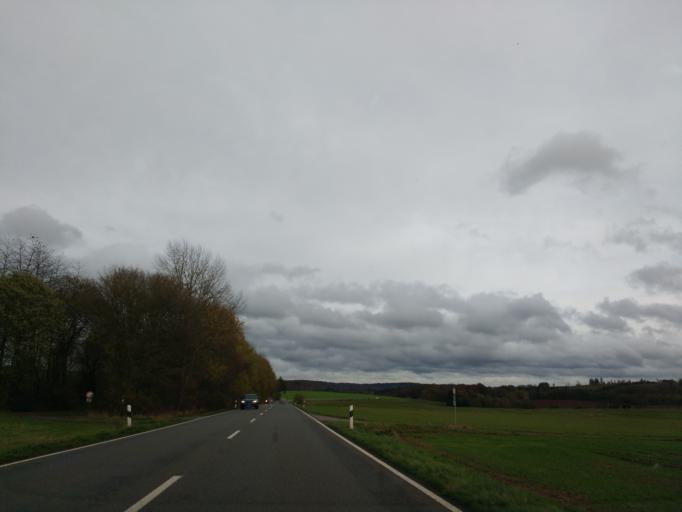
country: DE
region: Hesse
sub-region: Regierungsbezirk Kassel
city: Sachsenhausen
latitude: 51.2398
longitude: 9.0301
